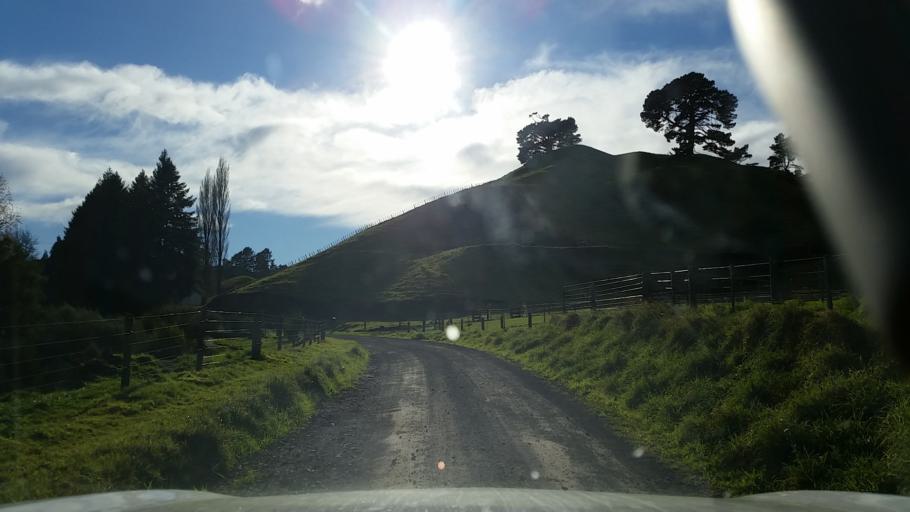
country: NZ
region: Waikato
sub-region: South Waikato District
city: Tokoroa
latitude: -38.3693
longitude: 176.0888
